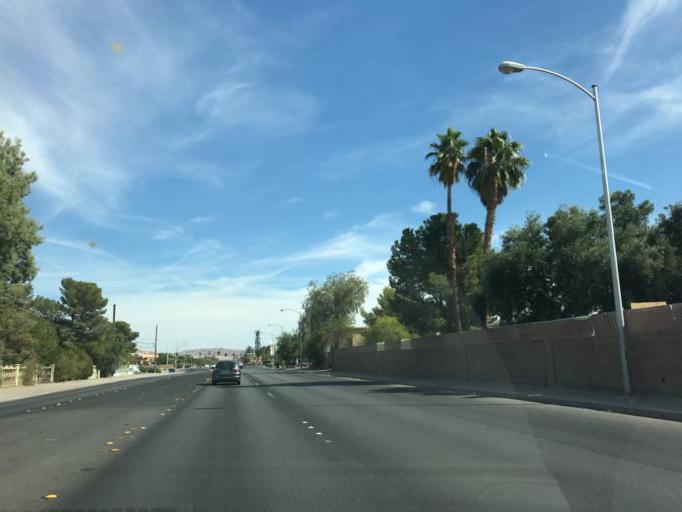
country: US
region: Nevada
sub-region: Clark County
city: Winchester
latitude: 36.1296
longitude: -115.0684
